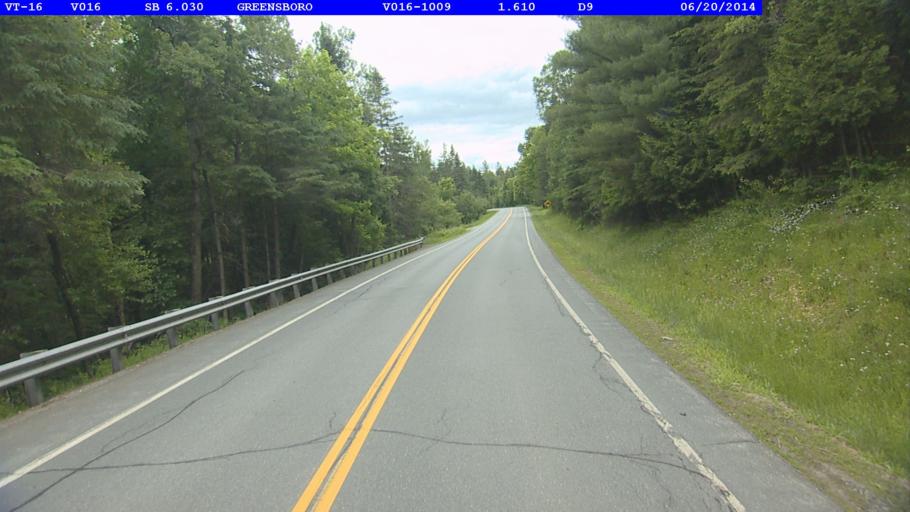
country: US
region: Vermont
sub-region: Caledonia County
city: Hardwick
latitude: 44.5650
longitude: -72.2536
